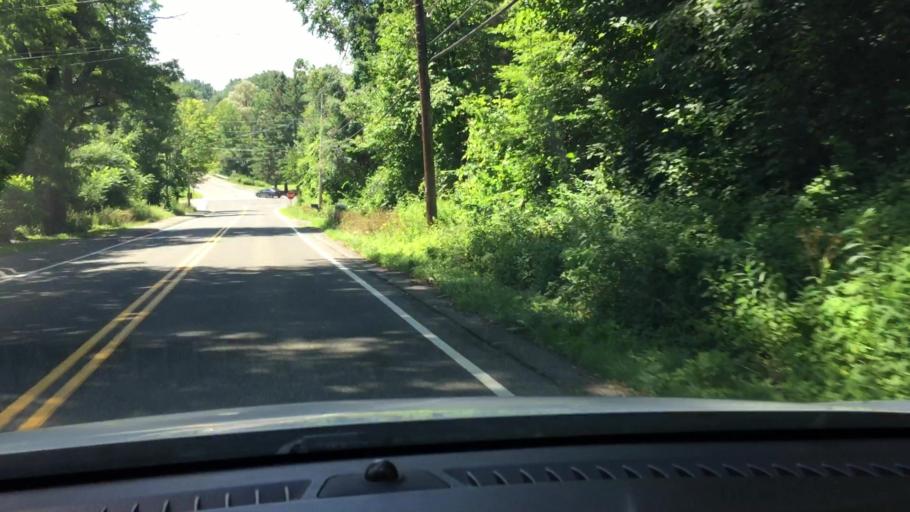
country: US
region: Massachusetts
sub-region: Berkshire County
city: Lenox
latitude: 42.3568
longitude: -73.2595
